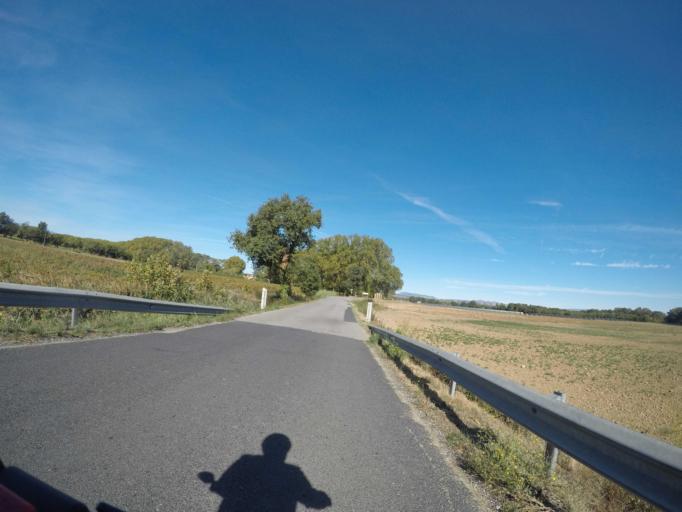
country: FR
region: Languedoc-Roussillon
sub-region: Departement des Pyrenees-Orientales
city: Le Soler
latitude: 42.6614
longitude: 2.7958
